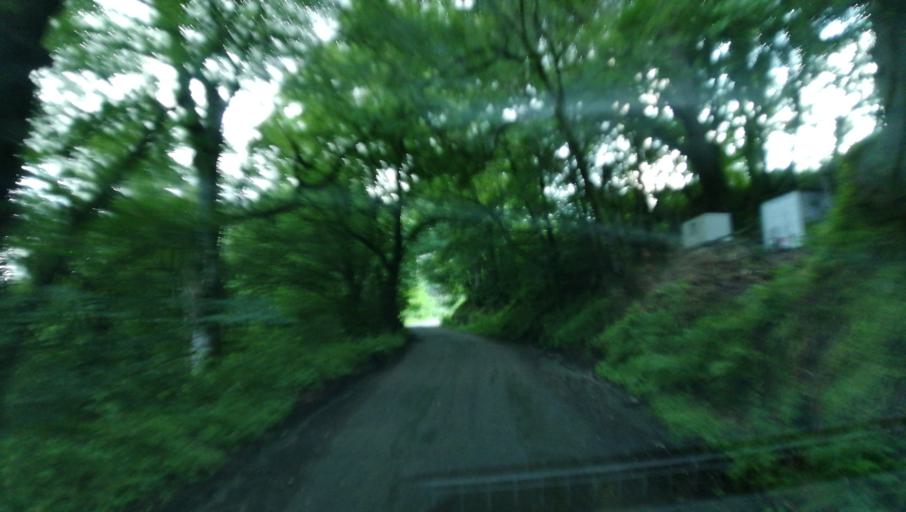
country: GB
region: Scotland
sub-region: Highland
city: Spean Bridge
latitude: 57.0690
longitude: -4.8204
